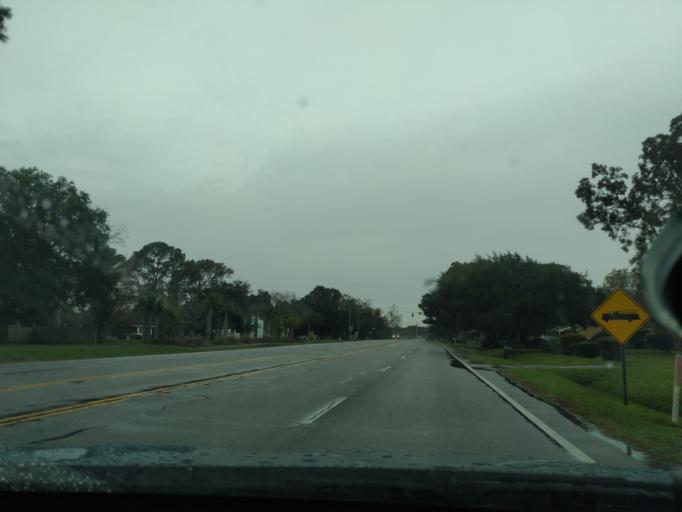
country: US
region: South Carolina
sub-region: Charleston County
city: Folly Beach
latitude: 32.6924
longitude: -79.9644
